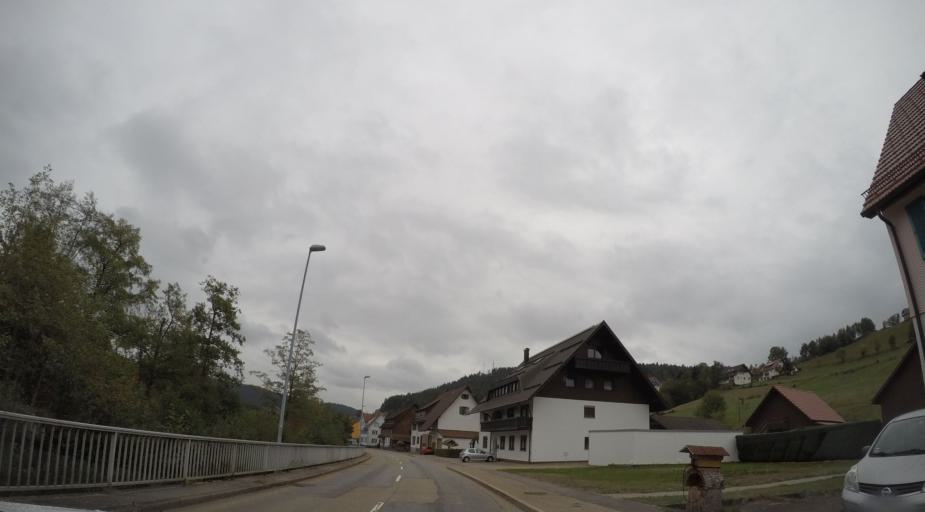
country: DE
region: Baden-Wuerttemberg
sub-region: Karlsruhe Region
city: Baiersbronn
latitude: 48.5271
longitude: 8.3627
